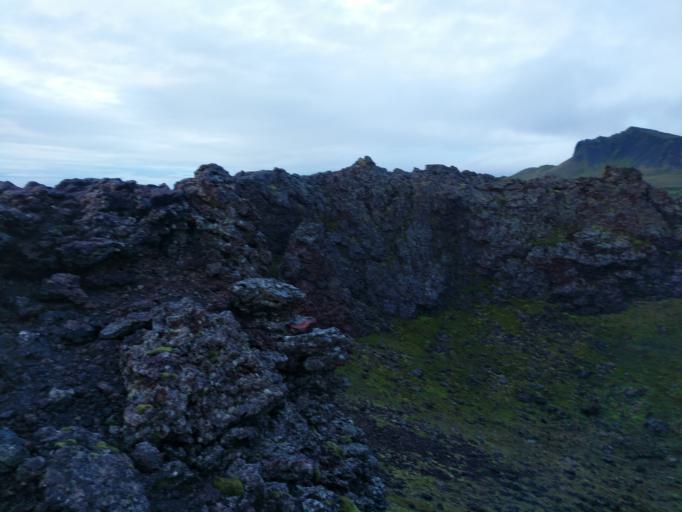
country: IS
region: West
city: Olafsvik
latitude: 64.8516
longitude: -23.9274
